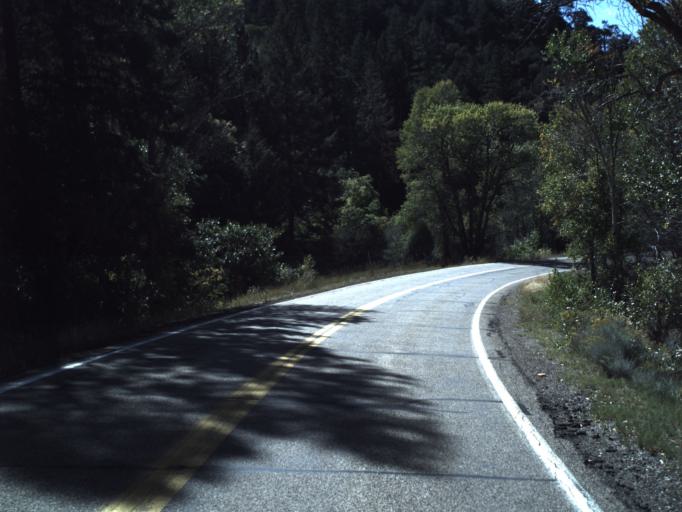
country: US
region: Utah
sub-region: Beaver County
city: Beaver
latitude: 38.2562
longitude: -112.5236
